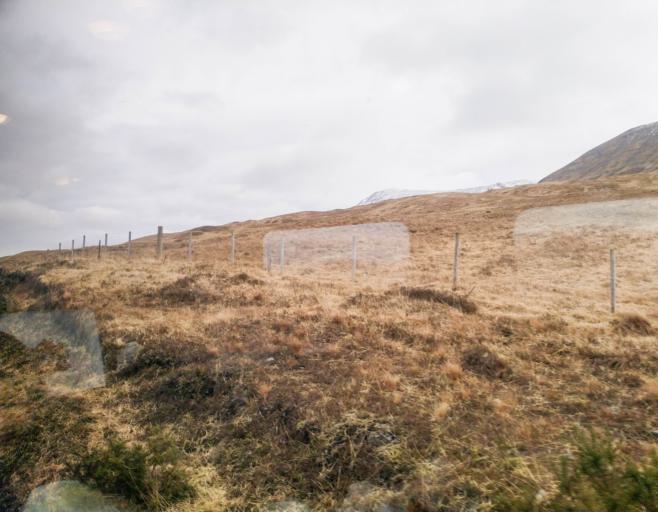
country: GB
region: Scotland
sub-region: Highland
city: Spean Bridge
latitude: 56.5370
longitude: -4.7619
